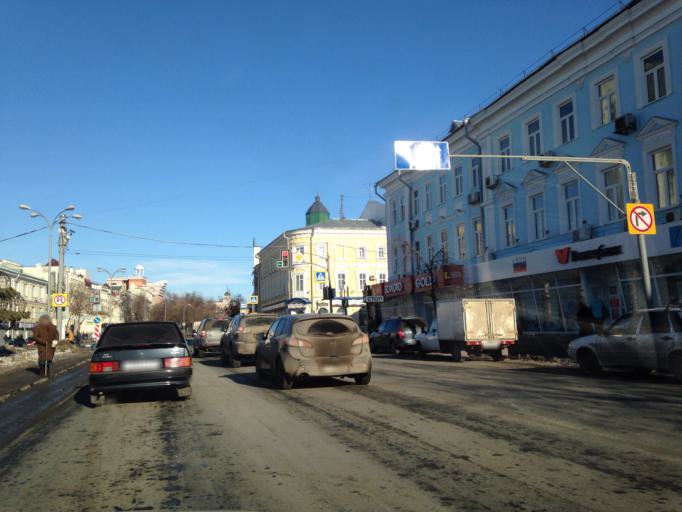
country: RU
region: Ulyanovsk
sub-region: Ulyanovskiy Rayon
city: Ulyanovsk
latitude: 54.3182
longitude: 48.3975
